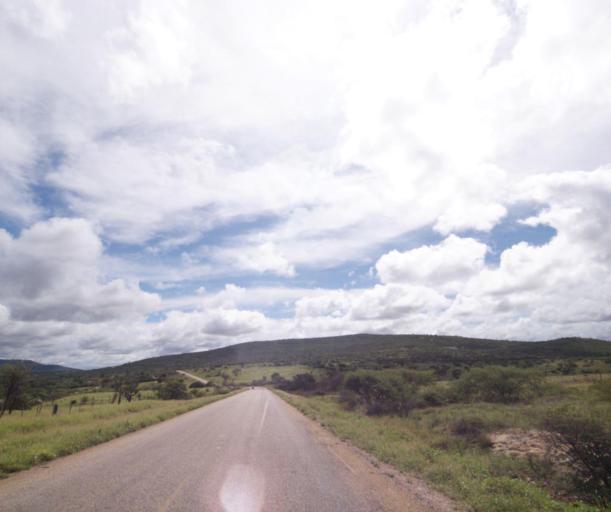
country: BR
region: Bahia
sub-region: Brumado
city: Brumado
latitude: -14.2119
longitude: -41.6333
